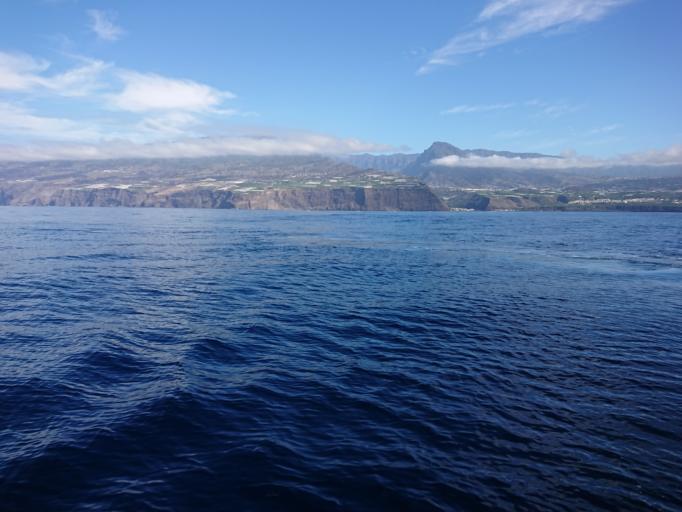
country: ES
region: Canary Islands
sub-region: Provincia de Santa Cruz de Tenerife
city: Tazacorte
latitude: 28.6272
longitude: -17.9964
